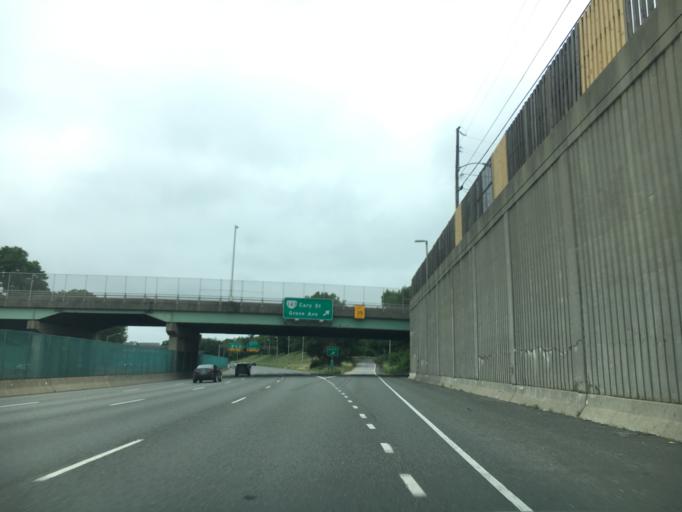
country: US
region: Virginia
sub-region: City of Richmond
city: Richmond
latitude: 37.5608
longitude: -77.4882
